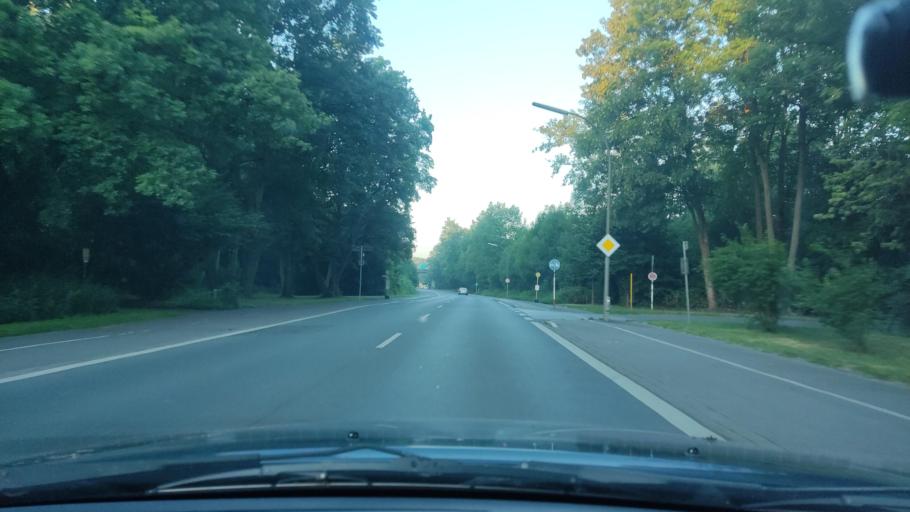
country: DE
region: North Rhine-Westphalia
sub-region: Regierungsbezirk Arnsberg
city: Dortmund
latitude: 51.5428
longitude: 7.4713
